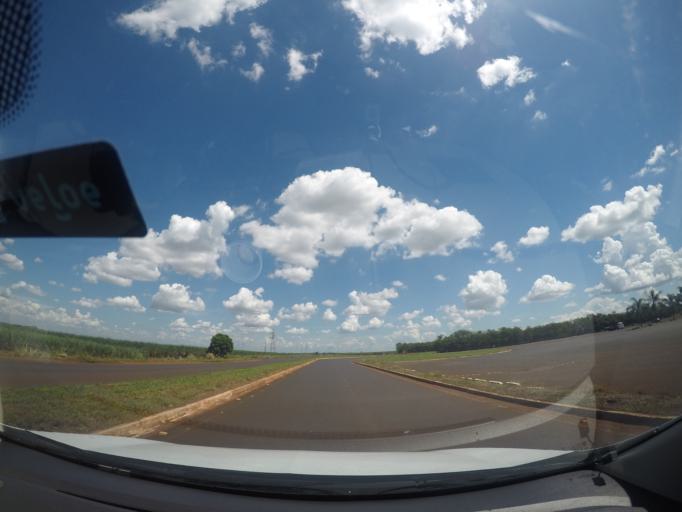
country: BR
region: Minas Gerais
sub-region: Frutal
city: Frutal
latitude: -19.8165
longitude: -48.7310
